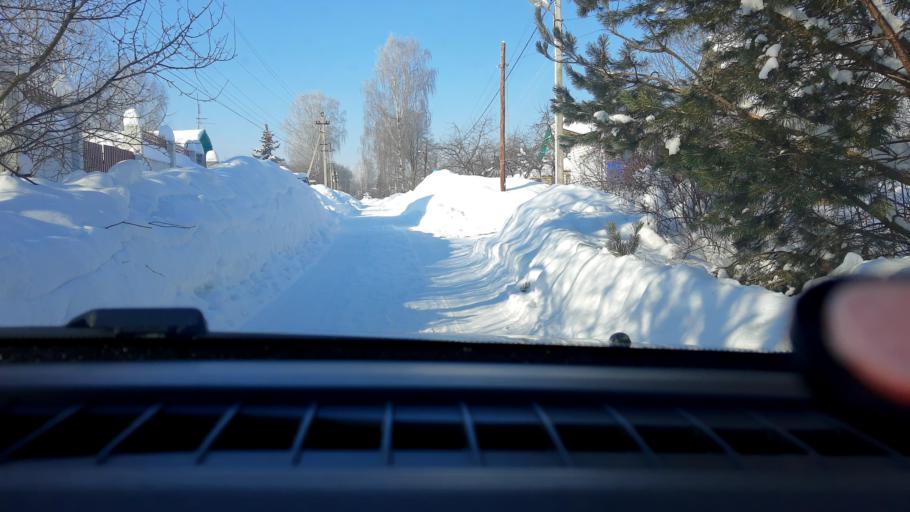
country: RU
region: Nizjnij Novgorod
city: Afonino
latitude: 56.1982
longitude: 44.0401
